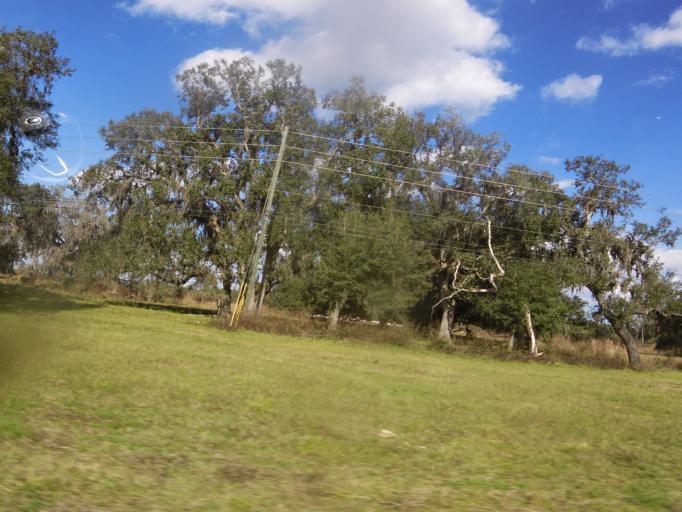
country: US
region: Florida
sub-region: Volusia County
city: De Leon Springs
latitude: 29.1412
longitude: -81.3623
